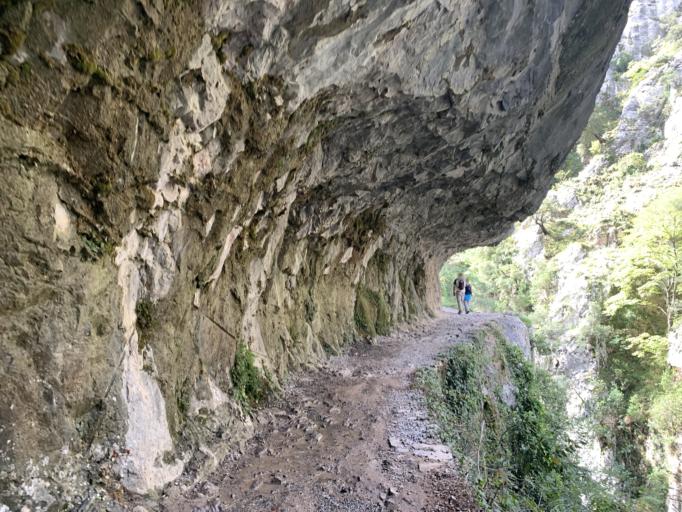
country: ES
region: Castille and Leon
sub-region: Provincia de Leon
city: Posada de Valdeon
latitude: 43.2260
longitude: -4.8961
